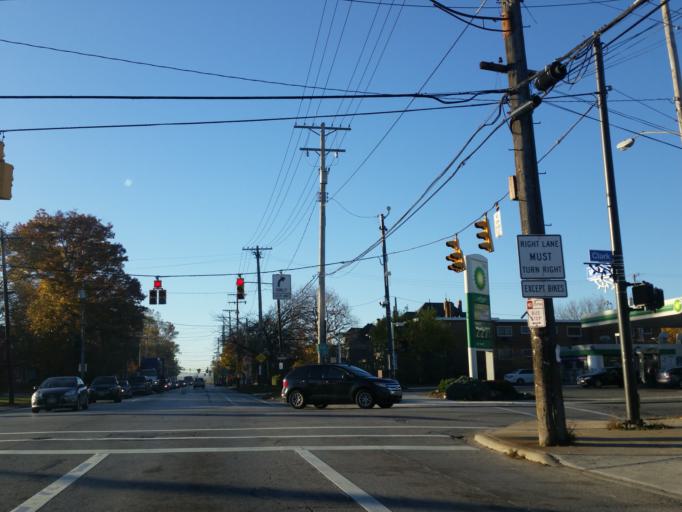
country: US
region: Ohio
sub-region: Cuyahoga County
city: Cleveland
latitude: 41.4703
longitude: -81.6913
